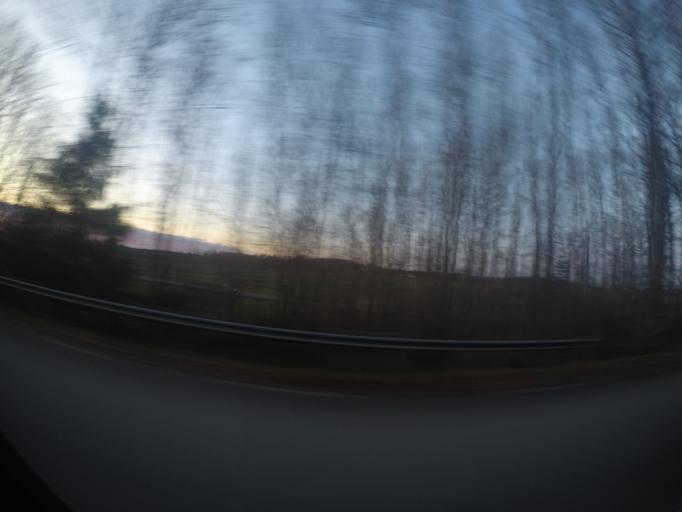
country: SE
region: OErebro
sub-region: Lindesbergs Kommun
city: Frovi
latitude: 59.3240
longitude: 15.4276
